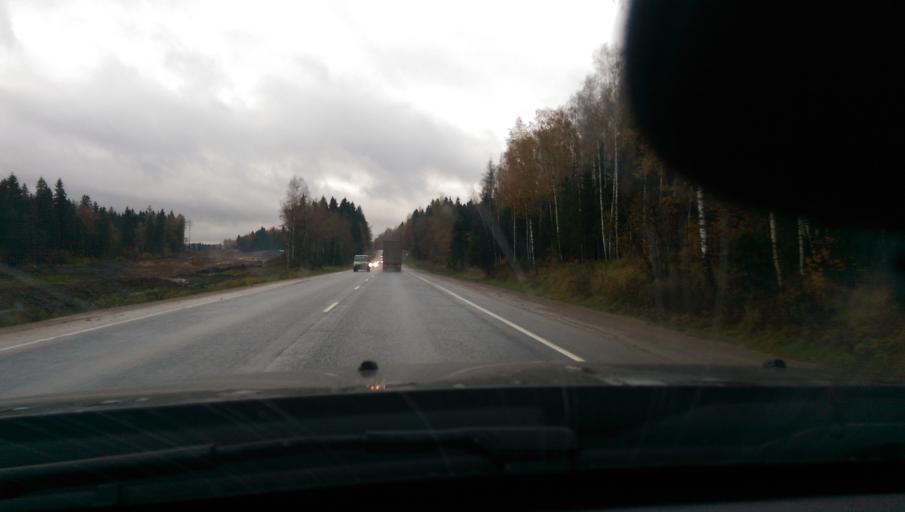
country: RU
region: Moskovskaya
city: Podosinki
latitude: 56.1736
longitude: 37.6587
